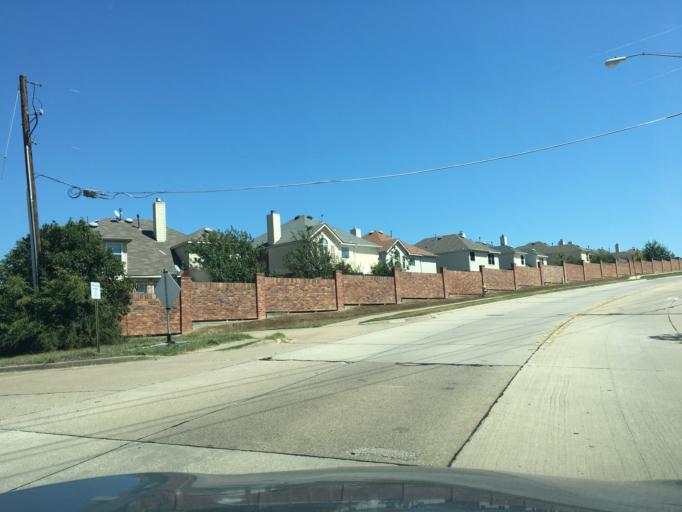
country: US
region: Texas
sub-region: Dallas County
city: Garland
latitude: 32.9512
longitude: -96.6459
